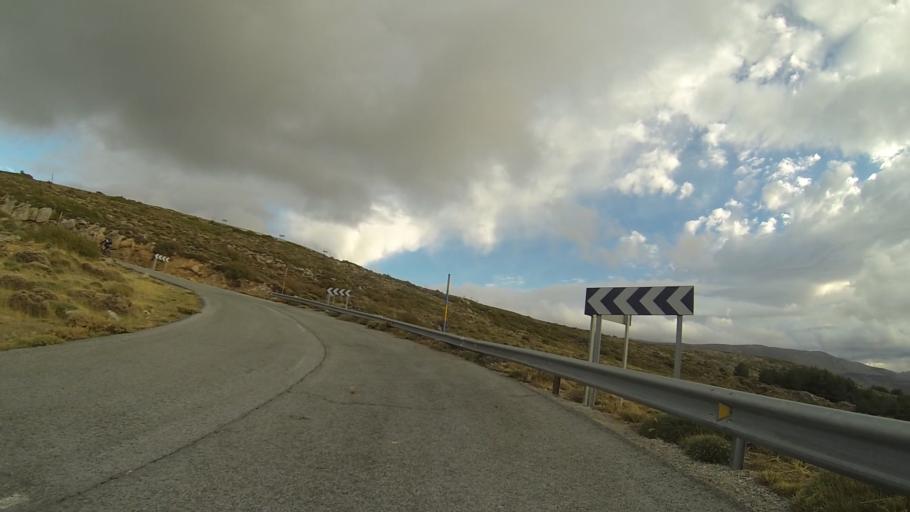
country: ES
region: Andalusia
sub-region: Provincia de Granada
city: Guejar-Sierra
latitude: 37.1213
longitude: -3.4329
